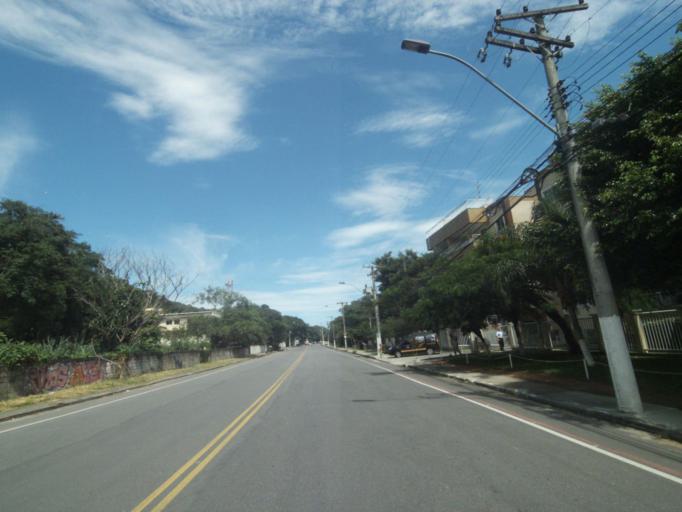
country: BR
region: Rio de Janeiro
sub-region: Niteroi
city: Niteroi
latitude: -22.9650
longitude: -43.0347
